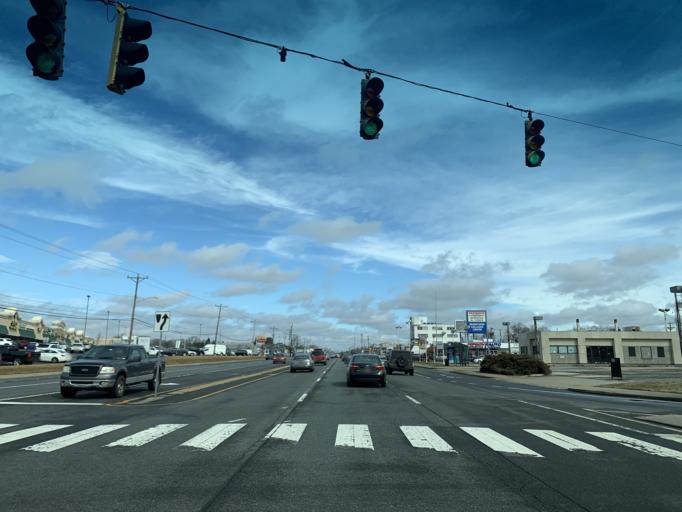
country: US
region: Delaware
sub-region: New Castle County
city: Pike Creek Valley
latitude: 39.7212
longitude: -75.6630
